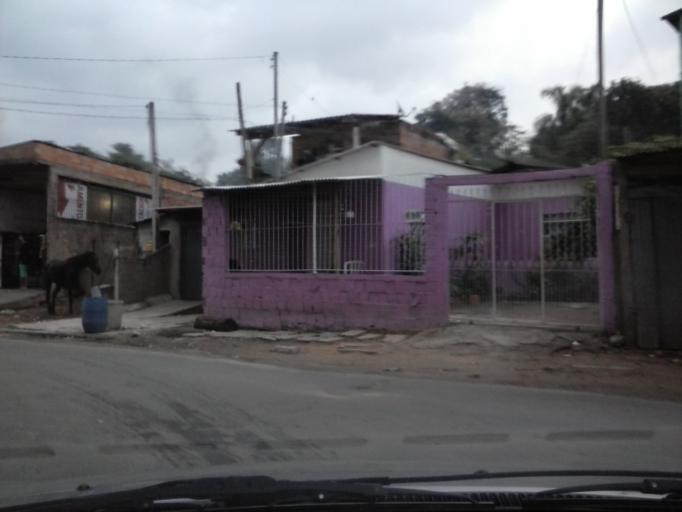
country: BR
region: Rio Grande do Sul
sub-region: Porto Alegre
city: Porto Alegre
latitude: -30.0509
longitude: -51.1592
